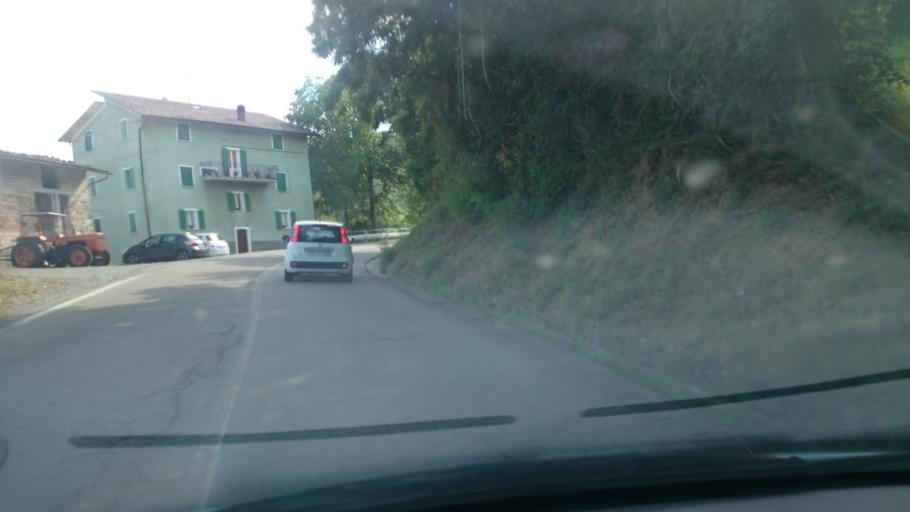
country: IT
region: Emilia-Romagna
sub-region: Provincia di Reggio Emilia
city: Villa Minozzo
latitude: 44.3577
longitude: 10.4614
